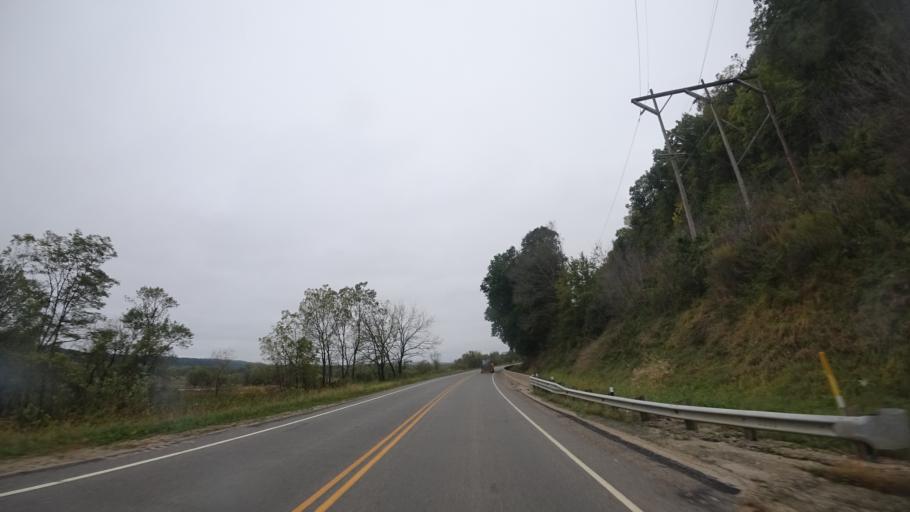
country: US
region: Wisconsin
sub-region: Crawford County
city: Prairie du Chien
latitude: 43.0776
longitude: -90.9316
